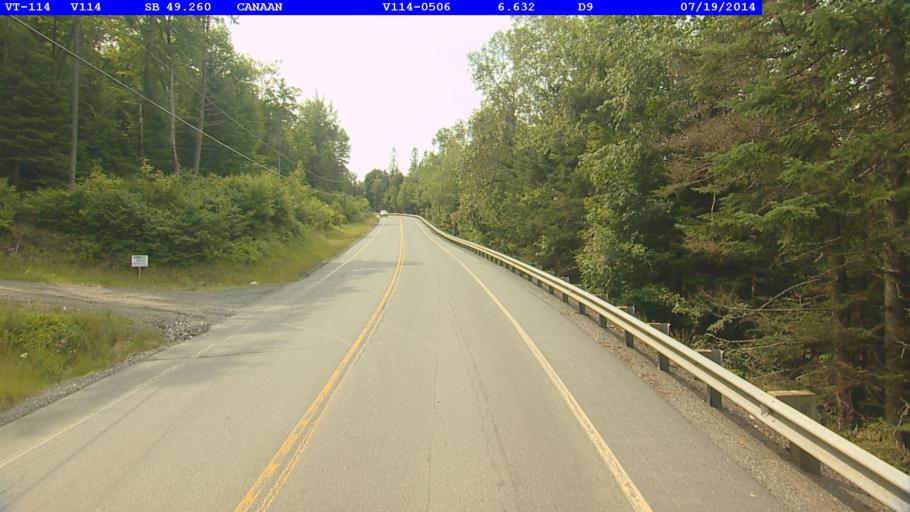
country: US
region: New Hampshire
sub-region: Coos County
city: Colebrook
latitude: 45.0092
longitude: -71.5633
